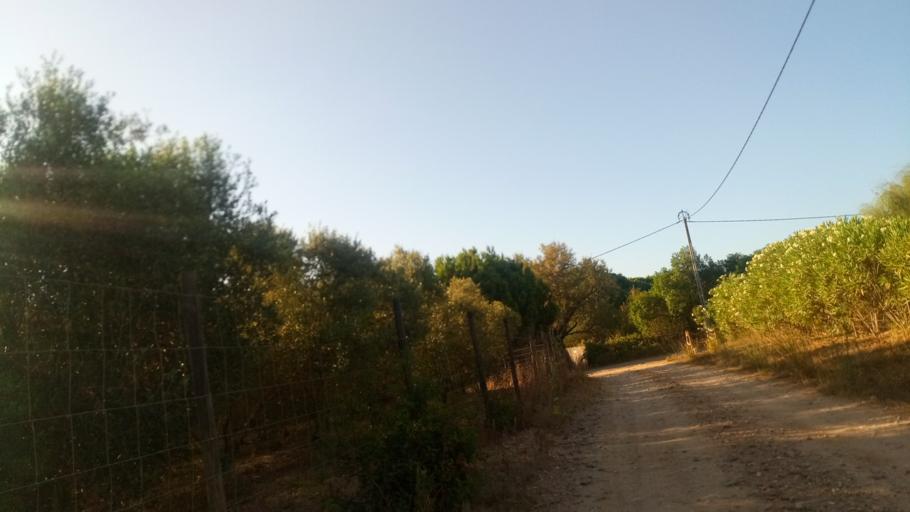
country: PT
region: Faro
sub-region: Tavira
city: Tavira
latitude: 37.1441
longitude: -7.5827
